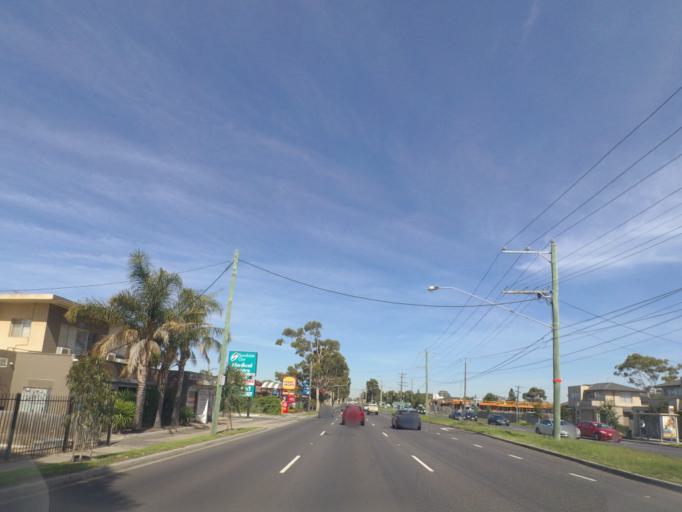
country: AU
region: Victoria
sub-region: Brimbank
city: Albion
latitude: -37.7786
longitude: 144.8418
